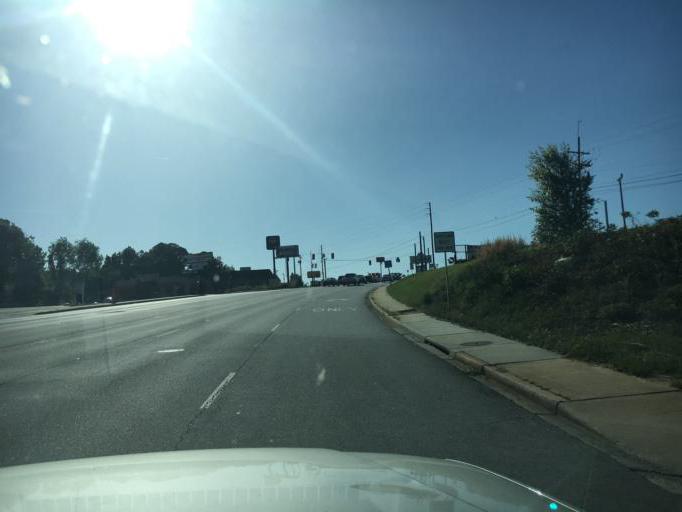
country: US
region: South Carolina
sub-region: Lexington County
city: Saint Andrews
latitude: 34.0443
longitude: -81.1208
